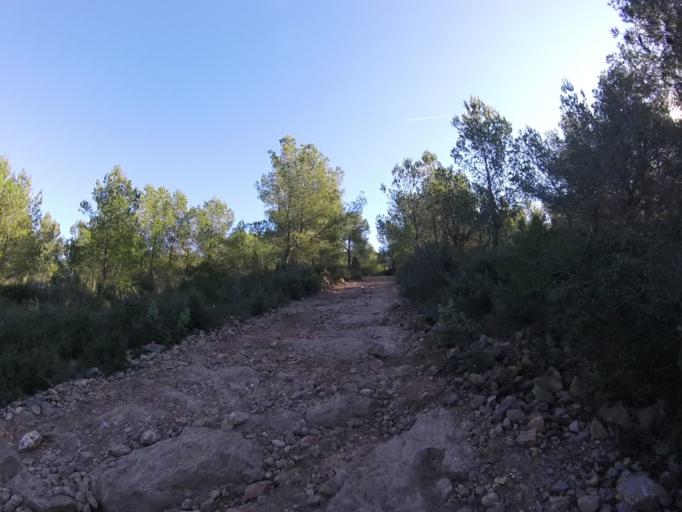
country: ES
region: Valencia
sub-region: Provincia de Castello
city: Benicassim
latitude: 40.0896
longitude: 0.0981
